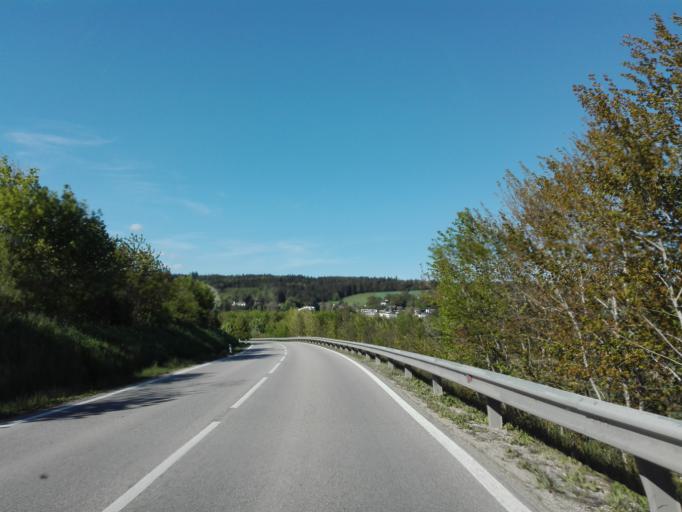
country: AT
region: Upper Austria
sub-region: Politischer Bezirk Perg
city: Perg
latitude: 48.2418
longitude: 14.6484
